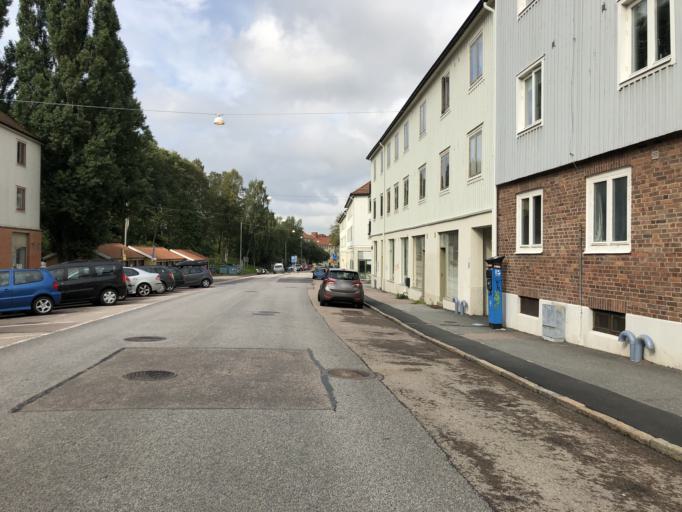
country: SE
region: Vaestra Goetaland
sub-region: Goteborg
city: Majorna
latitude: 57.6913
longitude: 11.9294
